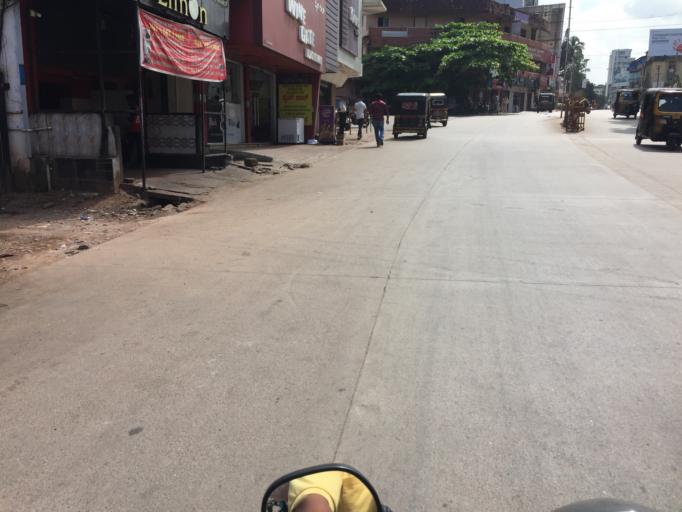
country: IN
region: Karnataka
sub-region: Dakshina Kannada
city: Mangalore
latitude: 12.8680
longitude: 74.8471
